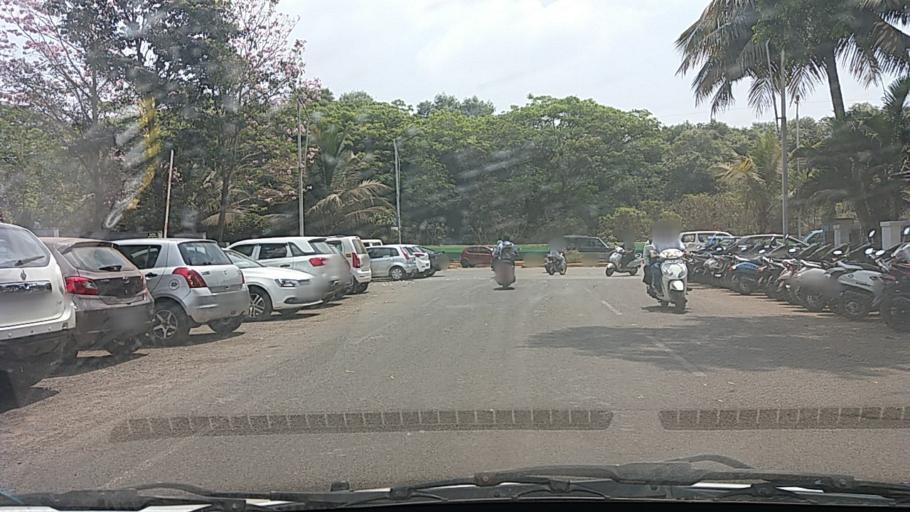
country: IN
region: Goa
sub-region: North Goa
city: Panaji
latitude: 15.4932
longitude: 73.8360
